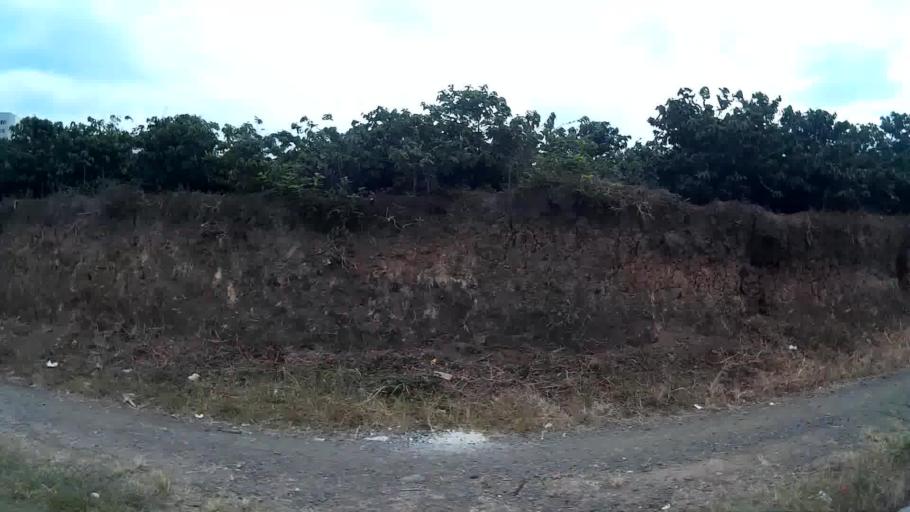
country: CO
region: Risaralda
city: Pereira
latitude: 4.7963
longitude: -75.7402
